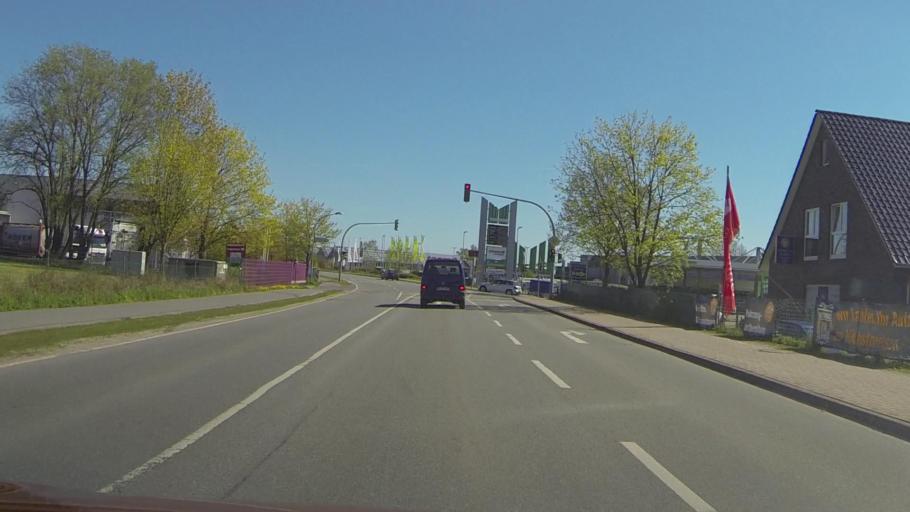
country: DE
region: Schleswig-Holstein
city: Kummerfeld
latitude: 53.6739
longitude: 9.7719
